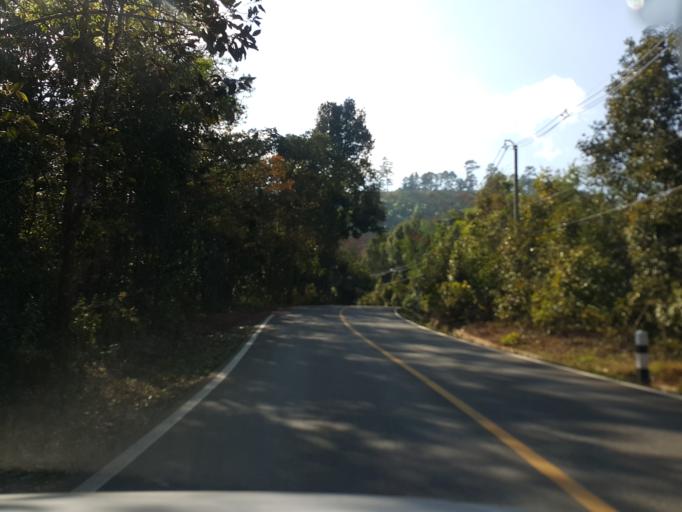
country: TH
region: Chiang Mai
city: Mae Wang
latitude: 18.6846
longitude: 98.5603
